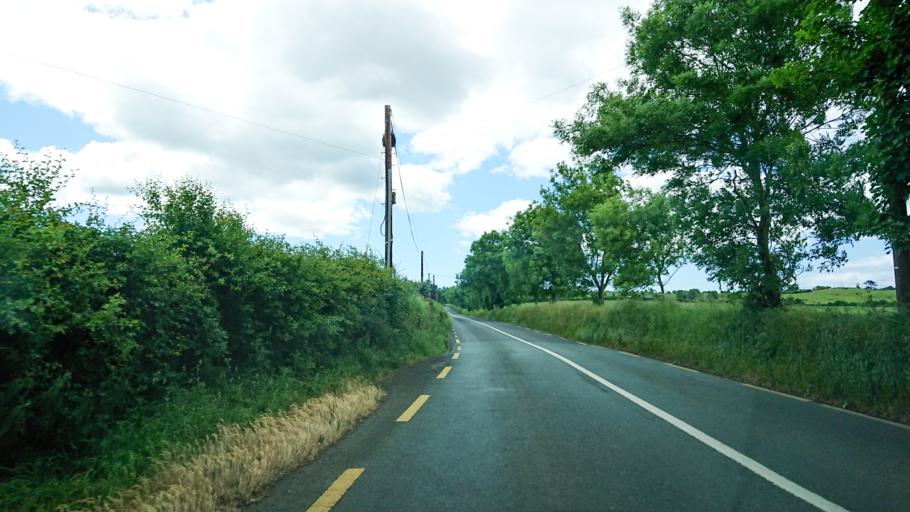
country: IE
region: Munster
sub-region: Waterford
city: Tra Mhor
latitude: 52.2207
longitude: -7.1985
